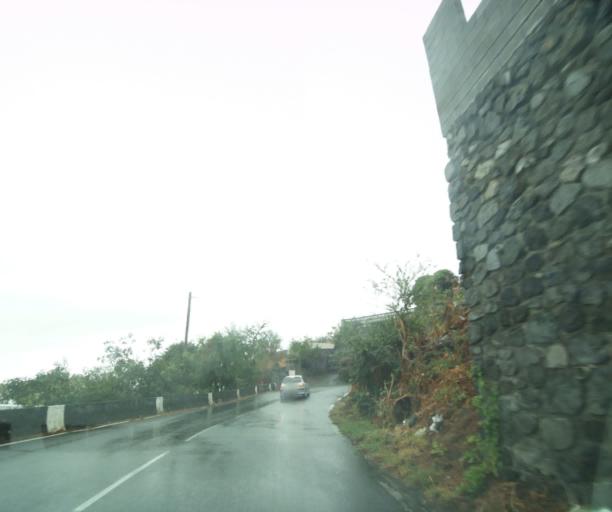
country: RE
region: Reunion
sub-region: Reunion
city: Saint-Paul
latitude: -21.0147
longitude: 55.2854
